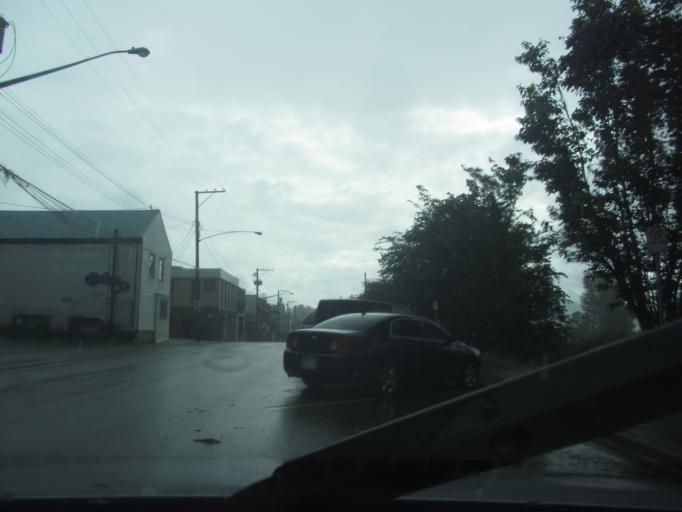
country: CA
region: British Columbia
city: Abbotsford
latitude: 49.1340
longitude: -122.3080
